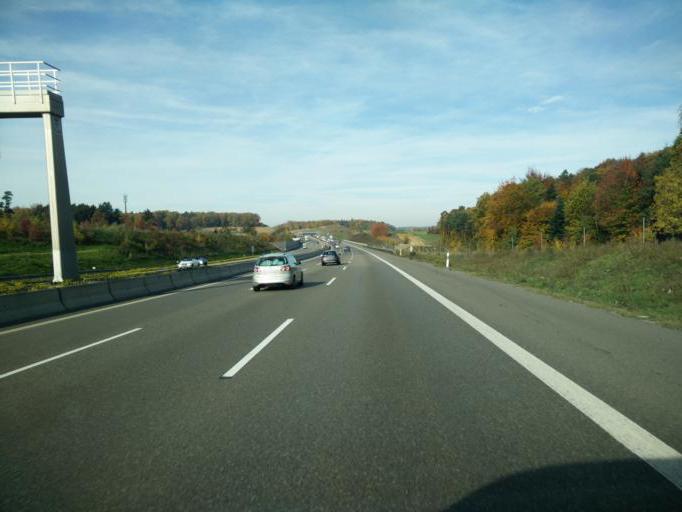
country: DE
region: Baden-Wuerttemberg
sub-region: Regierungsbezirk Stuttgart
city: Rutesheim
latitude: 48.8163
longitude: 8.9128
